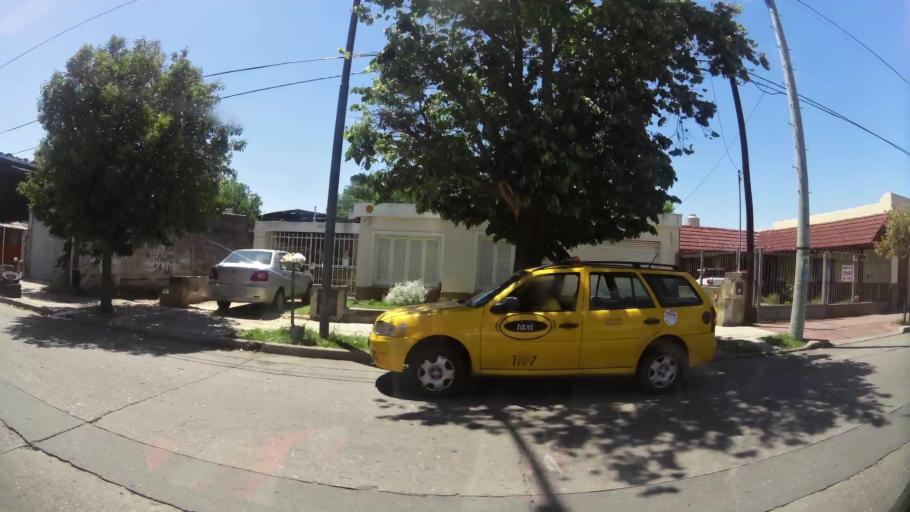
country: AR
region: Cordoba
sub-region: Departamento de Capital
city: Cordoba
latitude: -31.4174
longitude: -64.2267
